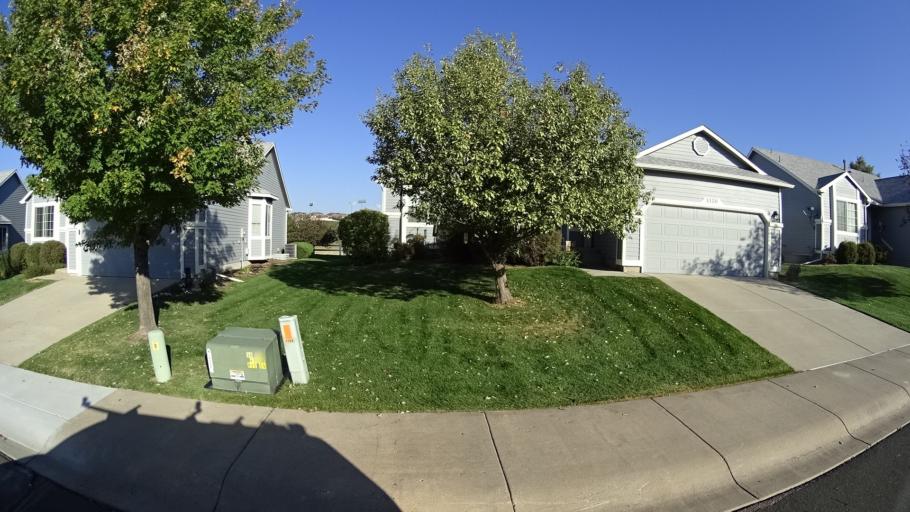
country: US
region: Colorado
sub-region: El Paso County
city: Cimarron Hills
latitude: 38.8918
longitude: -104.7075
